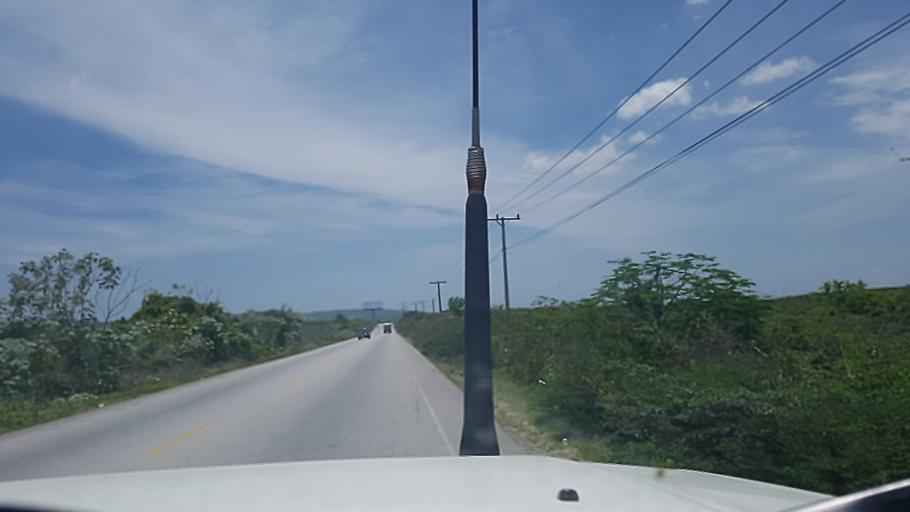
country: HT
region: Artibonite
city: Saint-Marc
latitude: 19.1518
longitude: -72.6293
